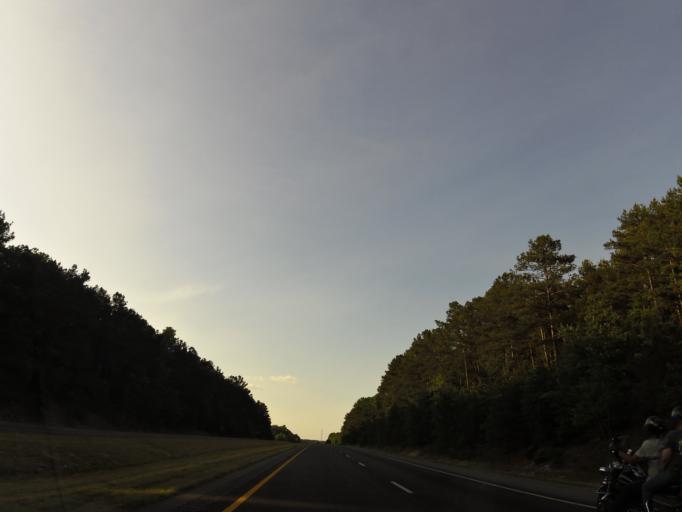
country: US
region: Alabama
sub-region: DeKalb County
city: Fort Payne
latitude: 34.5224
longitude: -85.6910
